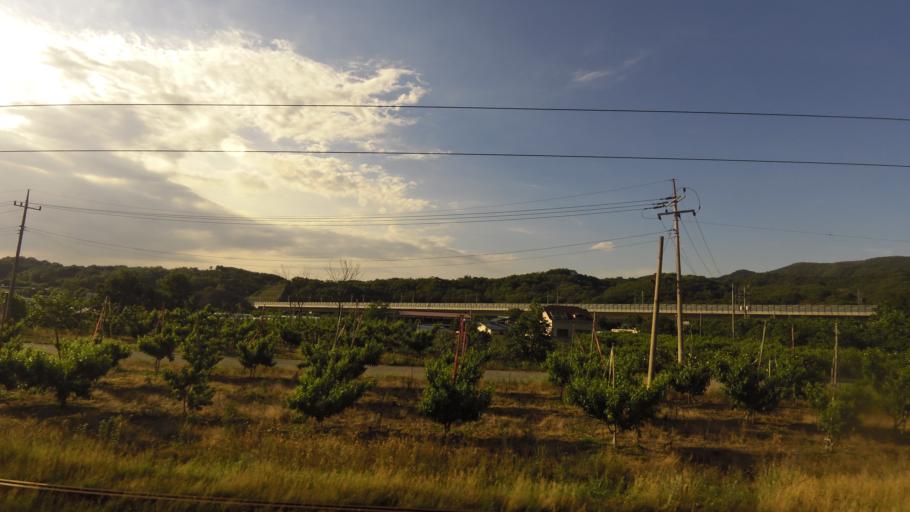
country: KR
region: Chungcheongbuk-do
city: Yong-dong
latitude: 36.1712
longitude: 127.7985
